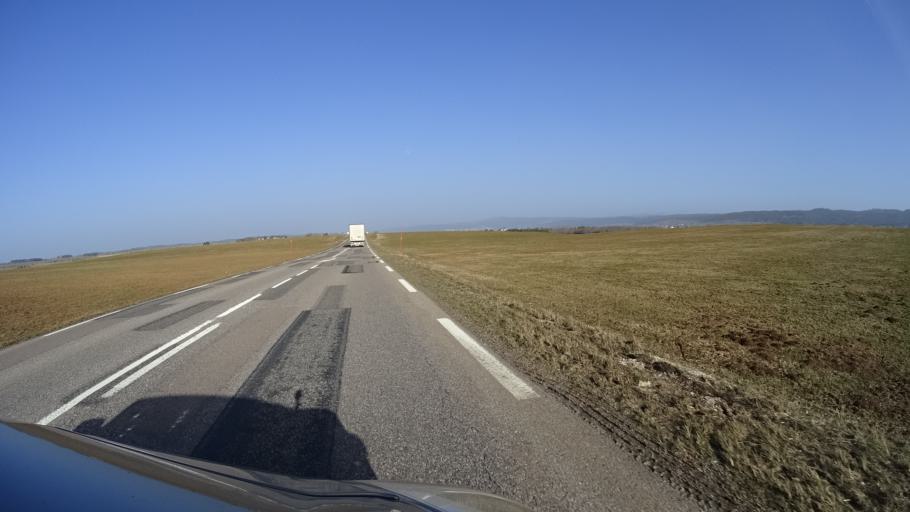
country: FR
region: Franche-Comte
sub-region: Departement du Doubs
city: Frasne
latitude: 46.8858
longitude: 6.2092
